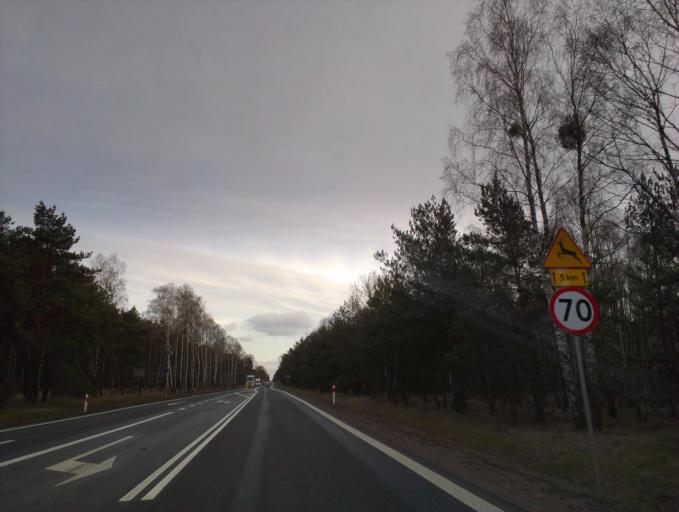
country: PL
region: Masovian Voivodeship
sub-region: Powiat sierpecki
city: Szczutowo
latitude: 52.8853
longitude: 19.5818
